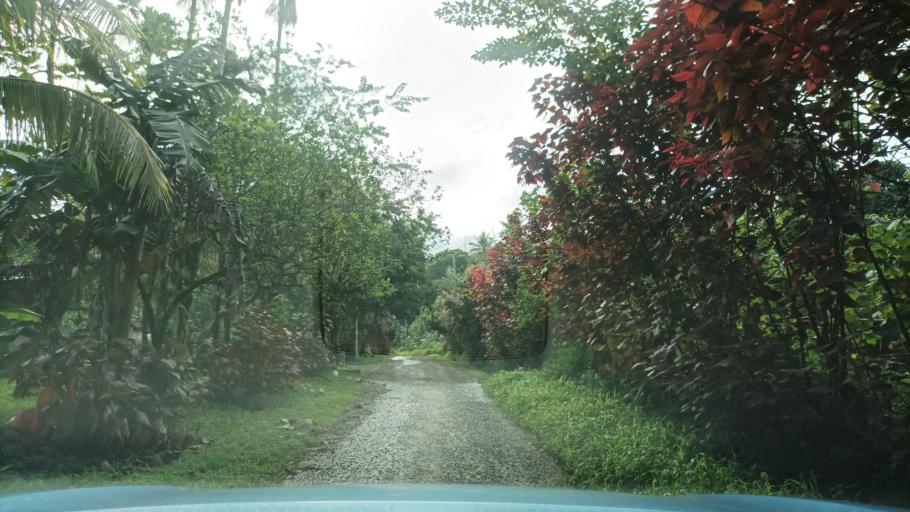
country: FM
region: Pohnpei
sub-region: Kolonia Municipality
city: Kolonia
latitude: 6.9312
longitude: 158.2374
